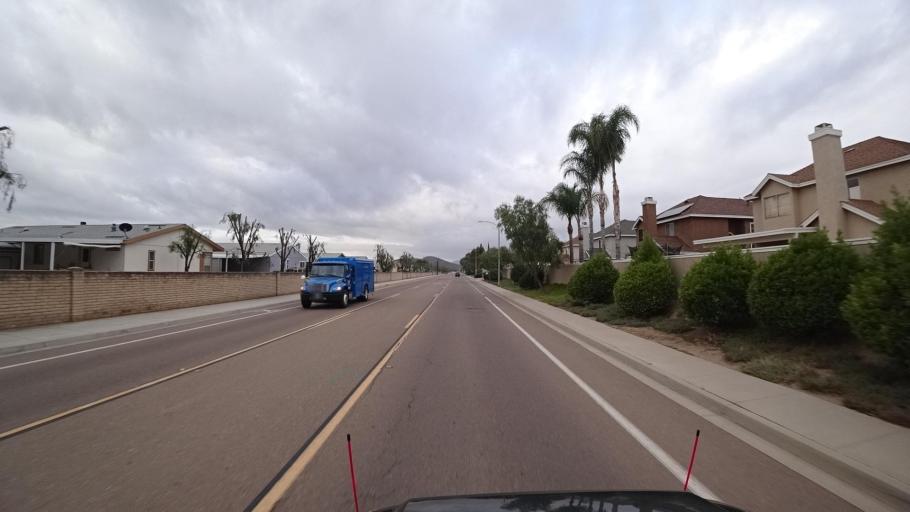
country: US
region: California
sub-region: San Diego County
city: Lakeside
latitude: 32.8644
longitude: -116.9379
